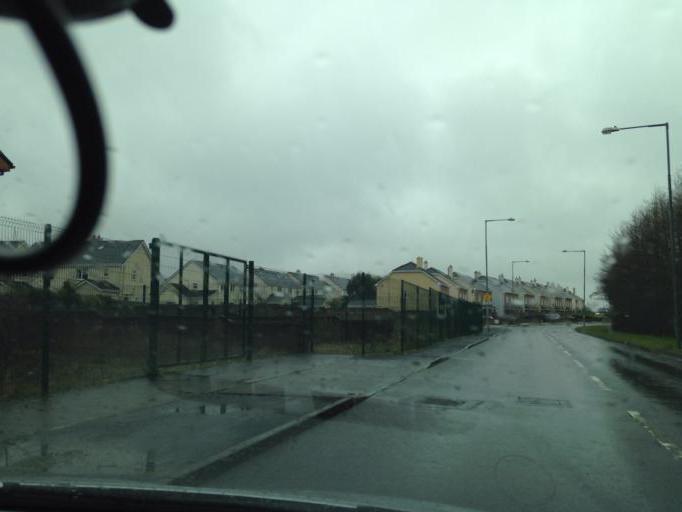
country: IE
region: Connaught
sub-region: County Galway
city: Gaillimh
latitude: 53.2726
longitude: -9.1008
